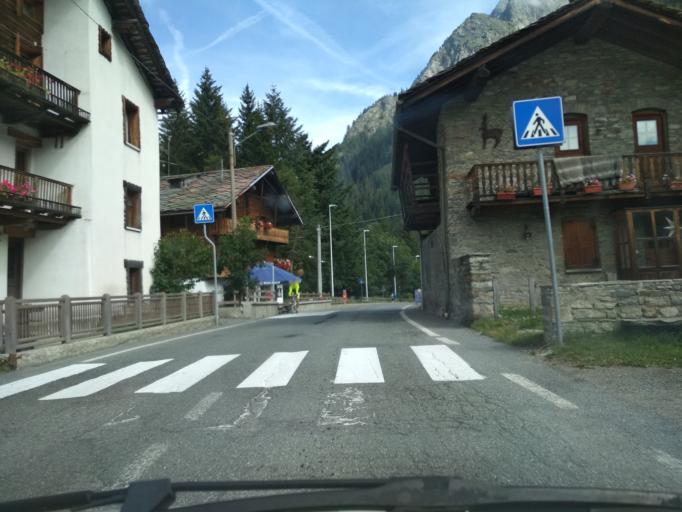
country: IT
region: Aosta Valley
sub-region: Valle d'Aosta
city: Gressoney-Saint-Jean
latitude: 45.7642
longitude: 7.8357
